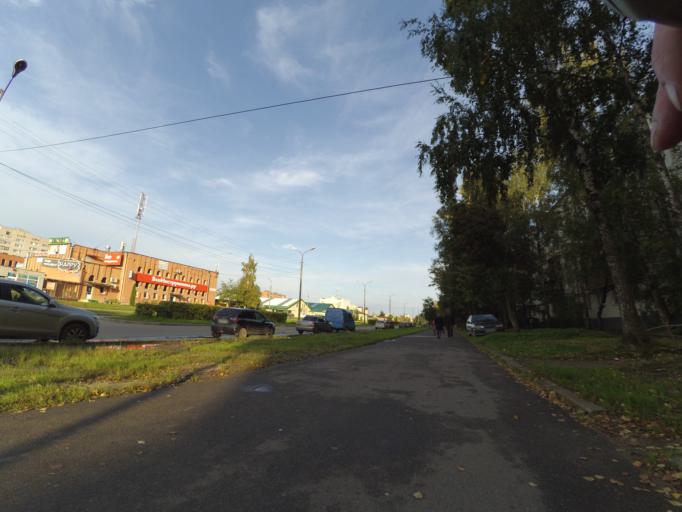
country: RU
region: Novgorod
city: Velikiy Novgorod
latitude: 58.5302
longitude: 31.2327
